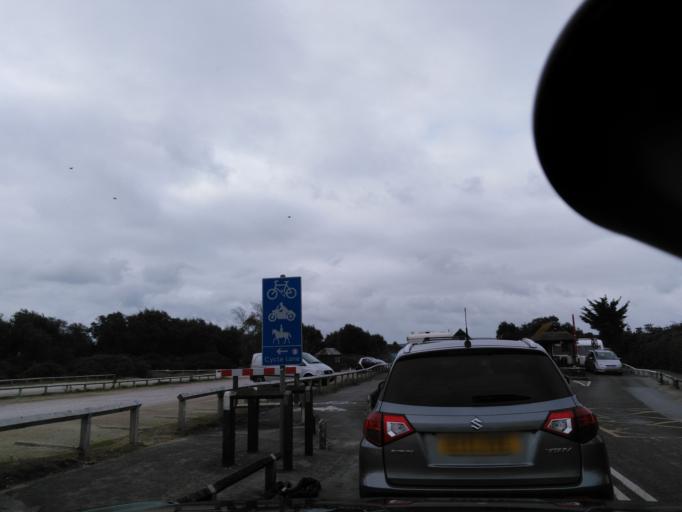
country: GB
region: England
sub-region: Dorset
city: Parkstone
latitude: 50.6770
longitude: -1.9518
